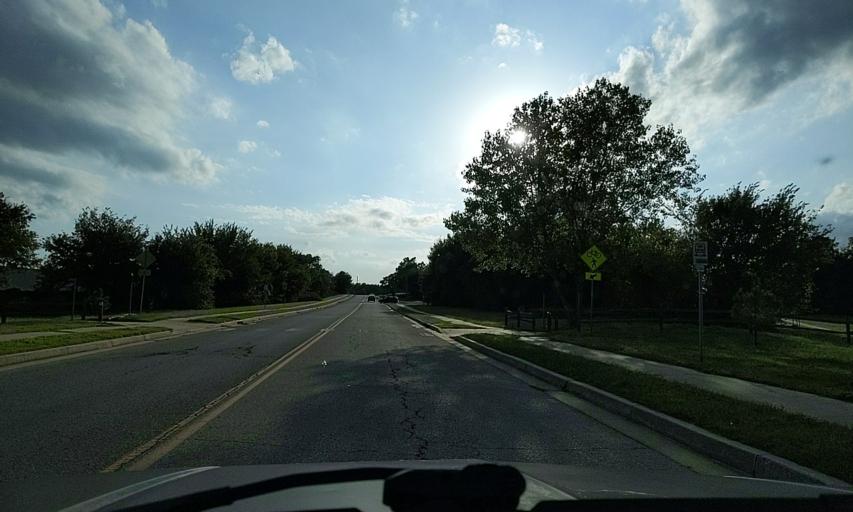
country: US
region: Oklahoma
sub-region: Tulsa County
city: Tulsa
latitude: 36.1950
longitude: -95.9806
